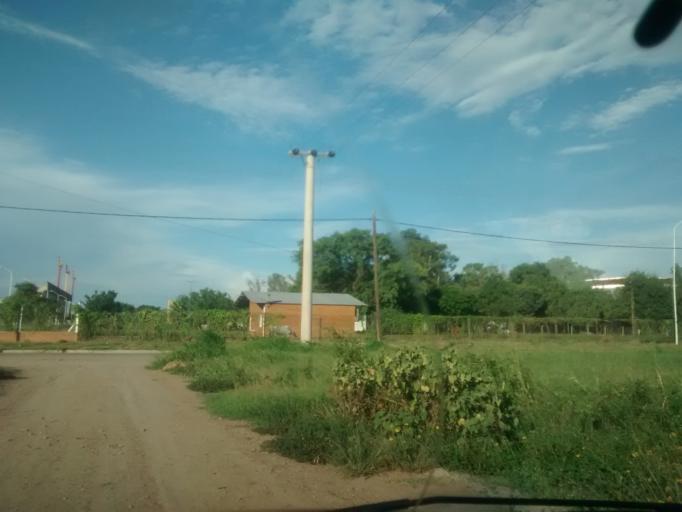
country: AR
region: Chaco
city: Fontana
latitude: -27.4459
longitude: -59.0122
